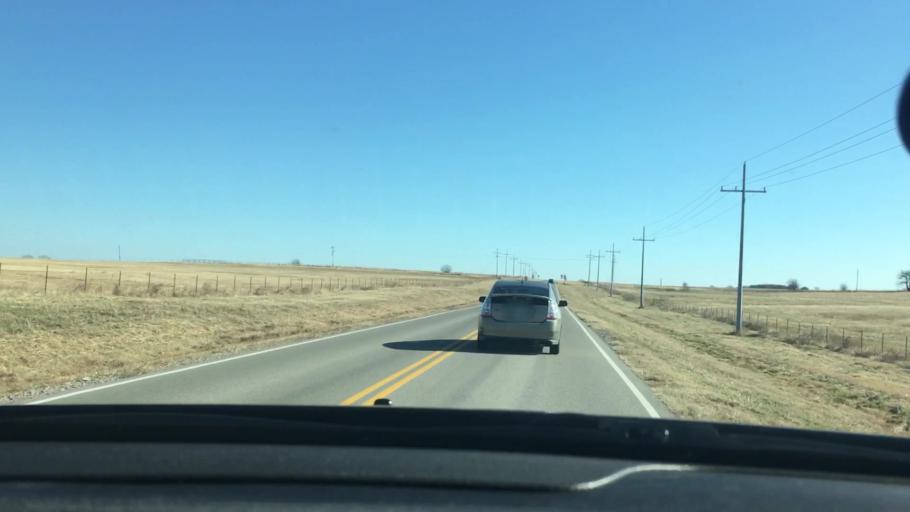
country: US
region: Oklahoma
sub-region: Murray County
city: Davis
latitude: 34.4773
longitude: -97.0945
